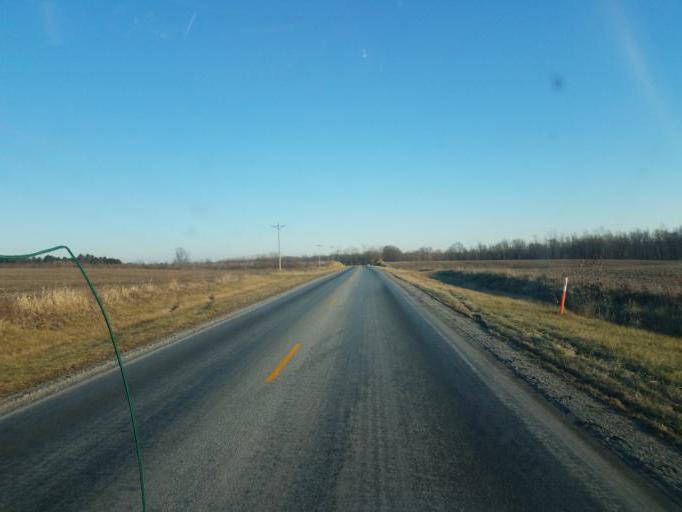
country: US
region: Ohio
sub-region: Hardin County
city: Kenton
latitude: 40.6261
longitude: -83.5342
